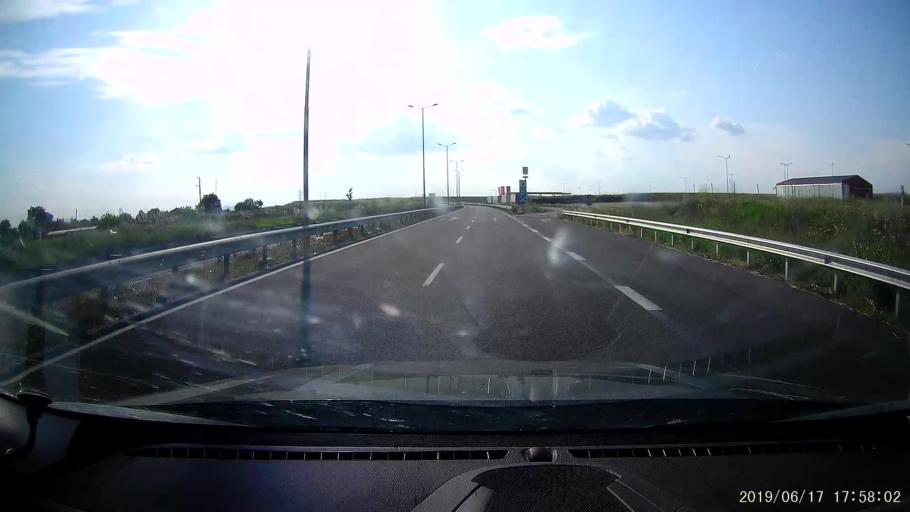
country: BG
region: Khaskovo
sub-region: Obshtina Svilengrad
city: Svilengrad
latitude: 41.7242
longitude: 26.3271
